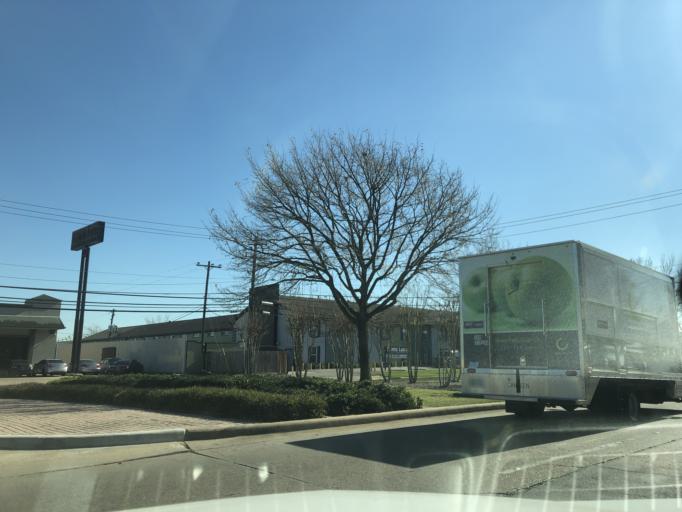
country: US
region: Texas
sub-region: Harris County
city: Bellaire
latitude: 29.6973
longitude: -95.4932
